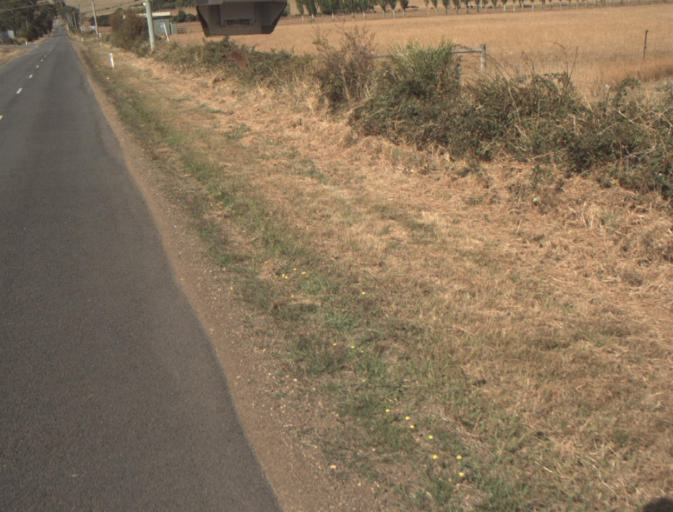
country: AU
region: Tasmania
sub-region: Launceston
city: Mayfield
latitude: -41.2512
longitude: 147.1476
